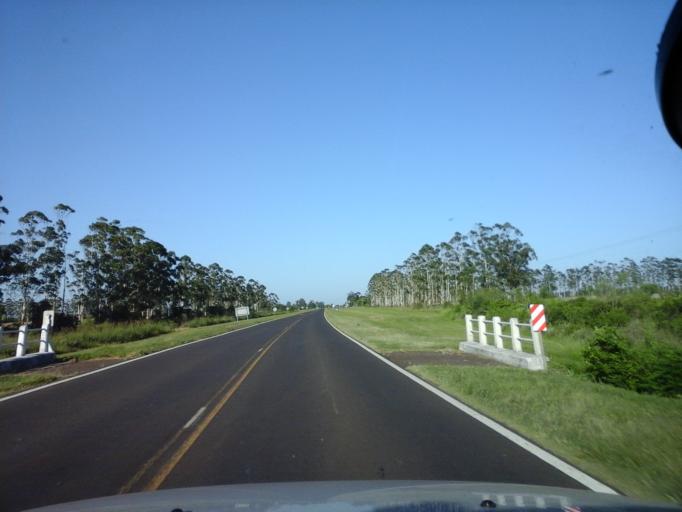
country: AR
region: Corrientes
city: Ita Ibate
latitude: -27.4408
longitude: -57.3554
